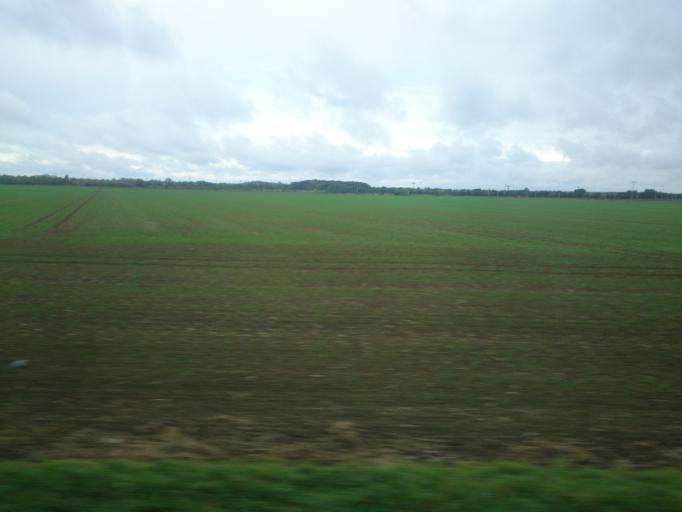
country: DE
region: Saxony-Anhalt
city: Grobers
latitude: 51.4227
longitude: 12.1295
